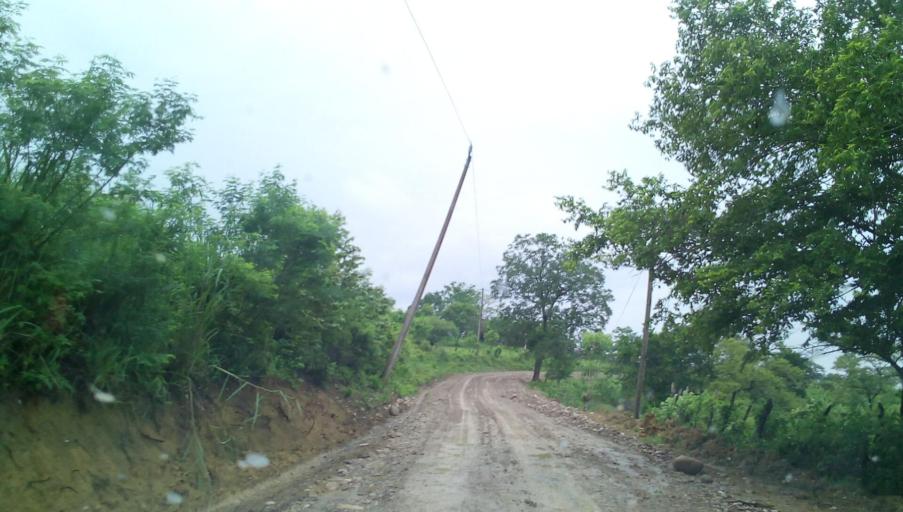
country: MX
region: Veracruz
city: Tempoal de Sanchez
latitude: 21.4538
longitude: -98.4260
